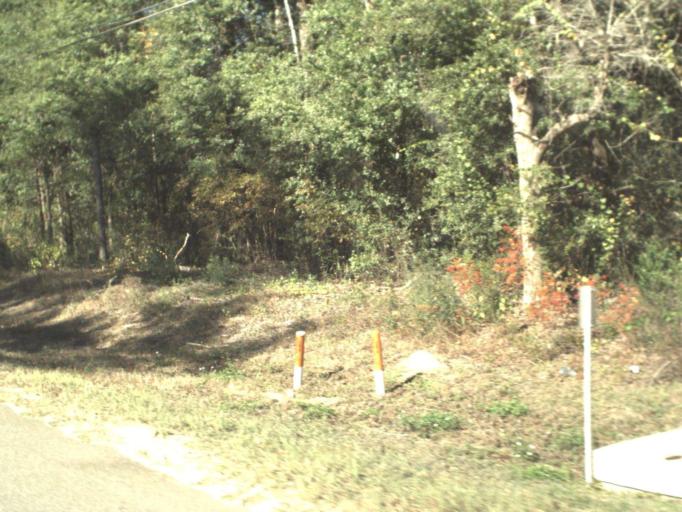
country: US
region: Florida
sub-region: Okaloosa County
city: Crestview
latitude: 30.7534
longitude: -86.6427
